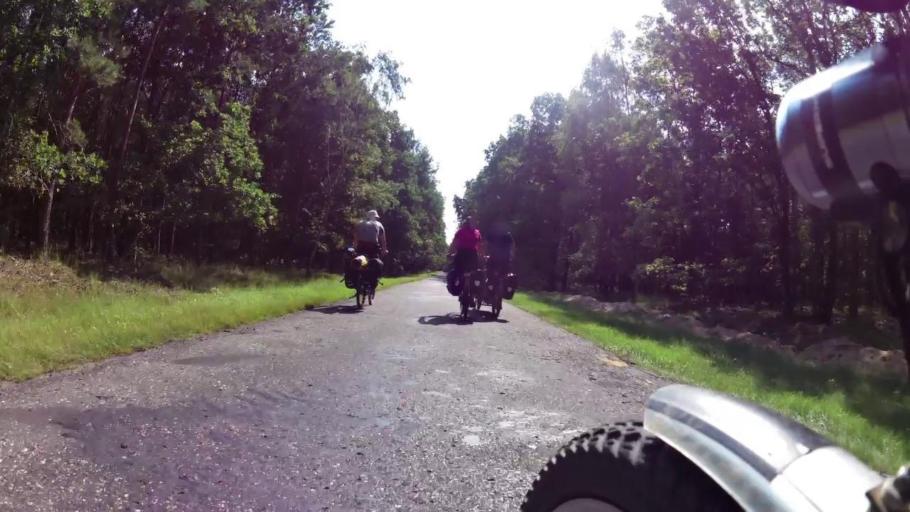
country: PL
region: West Pomeranian Voivodeship
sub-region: Powiat mysliborski
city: Boleszkowice
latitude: 52.6723
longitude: 14.5255
